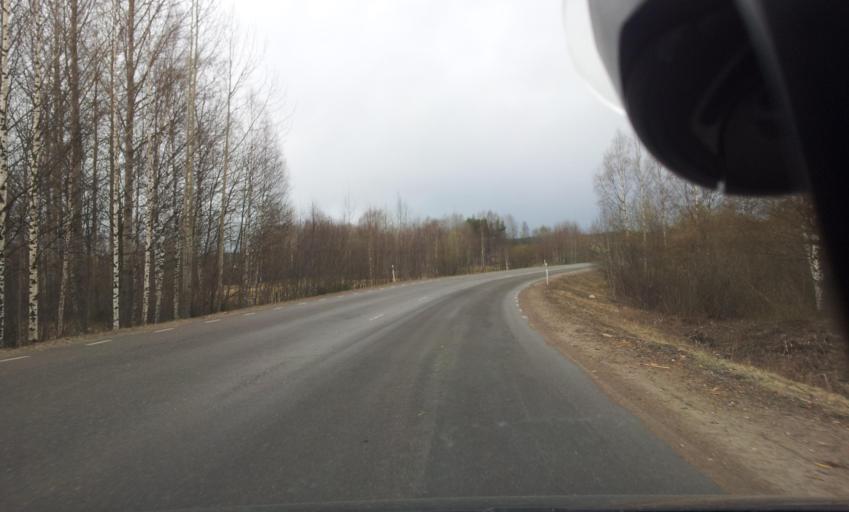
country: SE
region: Gaevleborg
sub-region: Ljusdals Kommun
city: Ljusdal
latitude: 61.8202
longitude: 16.1066
